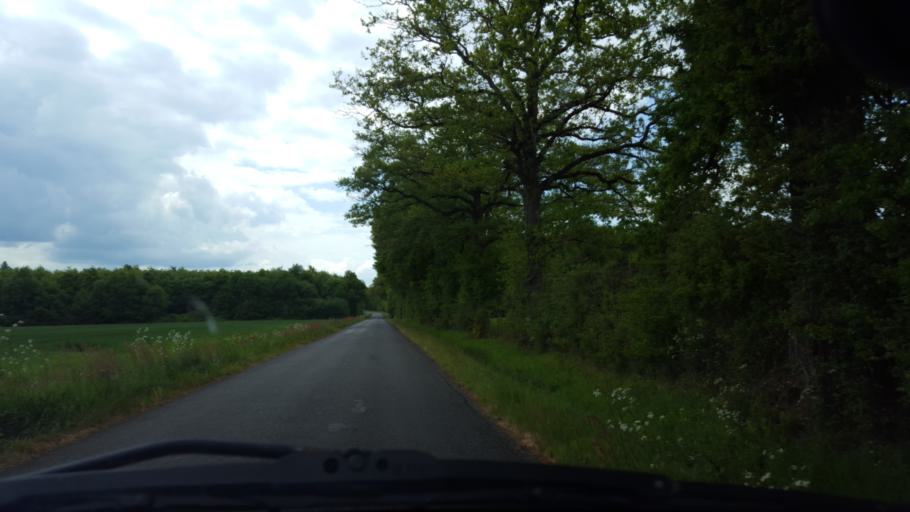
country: FR
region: Pays de la Loire
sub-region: Departement de la Loire-Atlantique
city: Saint-Philbert-de-Grand-Lieu
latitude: 47.0325
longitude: -1.6174
